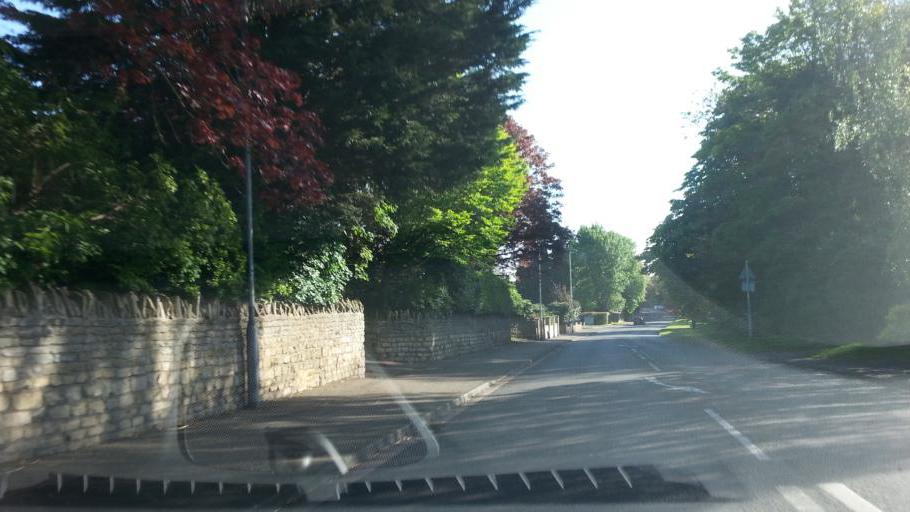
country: GB
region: England
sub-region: Peterborough
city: Peterborough
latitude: 52.5708
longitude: -0.2816
